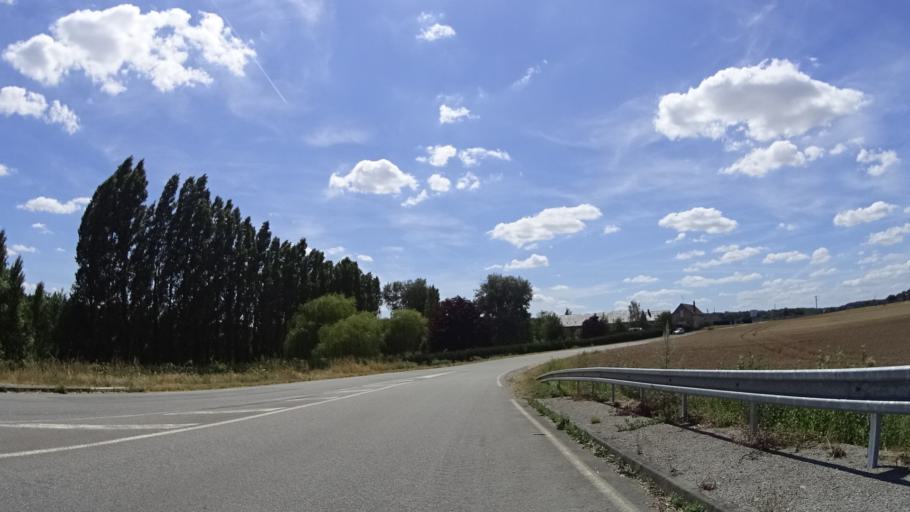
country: FR
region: Pays de la Loire
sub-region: Departement de Maine-et-Loire
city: Cande
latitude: 47.6135
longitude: -0.9862
